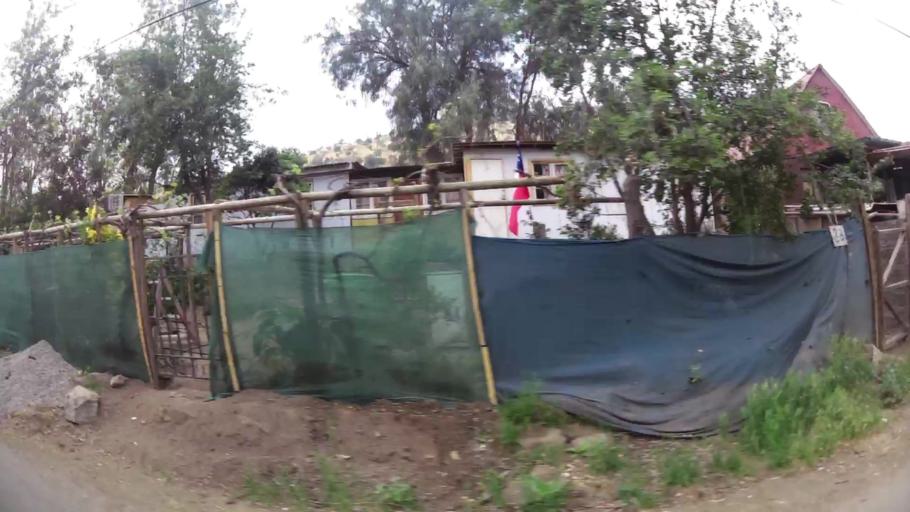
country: CL
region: Santiago Metropolitan
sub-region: Provincia de Chacabuco
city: Chicureo Abajo
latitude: -33.2383
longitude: -70.6738
